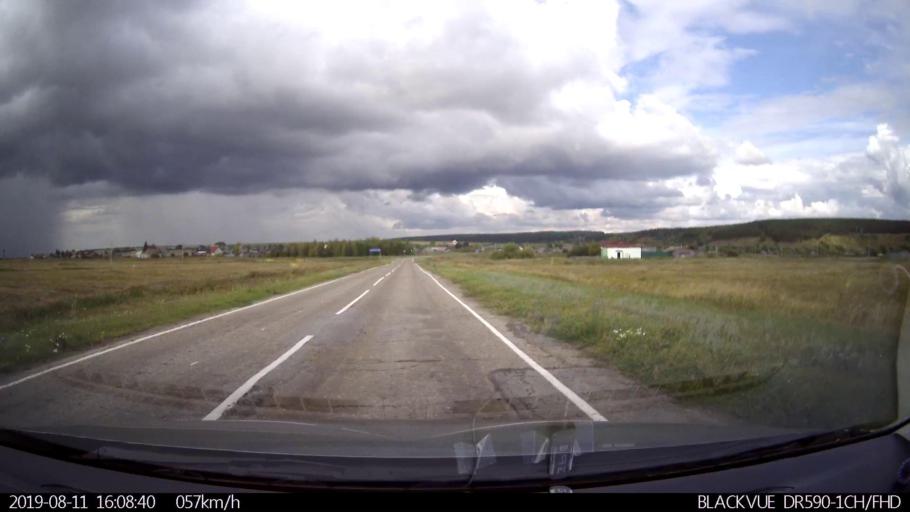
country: RU
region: Ulyanovsk
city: Ignatovka
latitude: 53.9867
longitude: 47.6489
